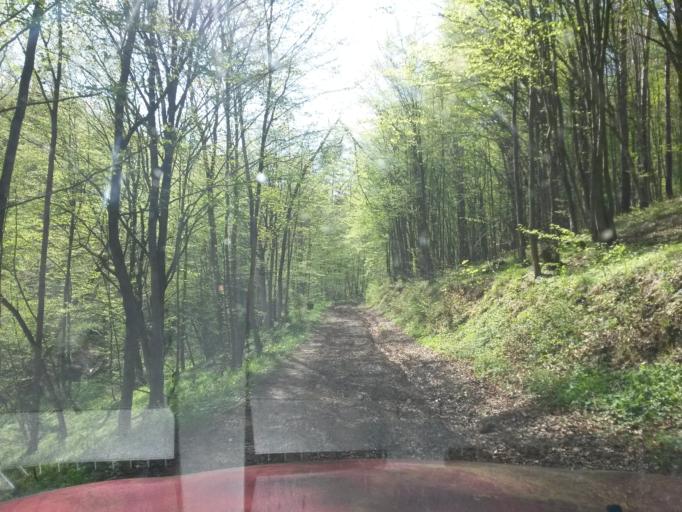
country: SK
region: Presovsky
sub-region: Okres Presov
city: Presov
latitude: 48.9464
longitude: 21.1591
